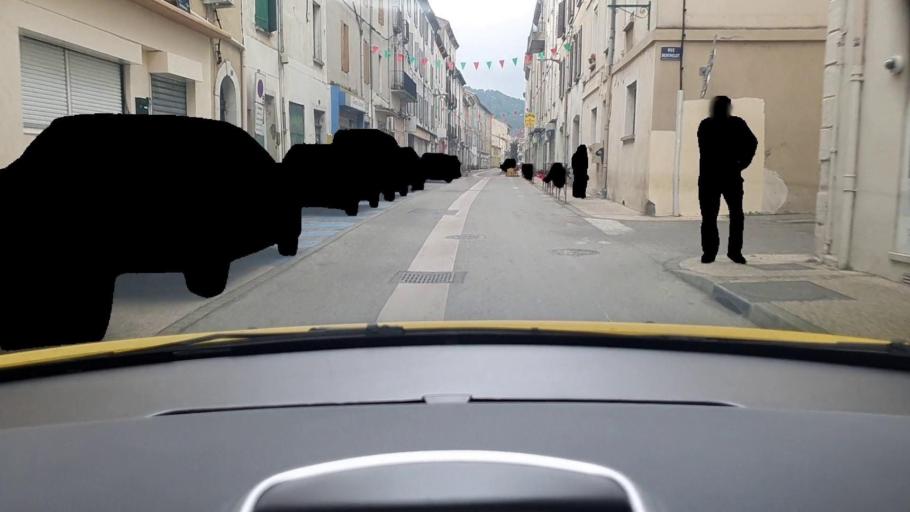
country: FR
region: Languedoc-Roussillon
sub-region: Departement du Gard
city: Besseges
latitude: 44.2910
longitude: 4.0985
